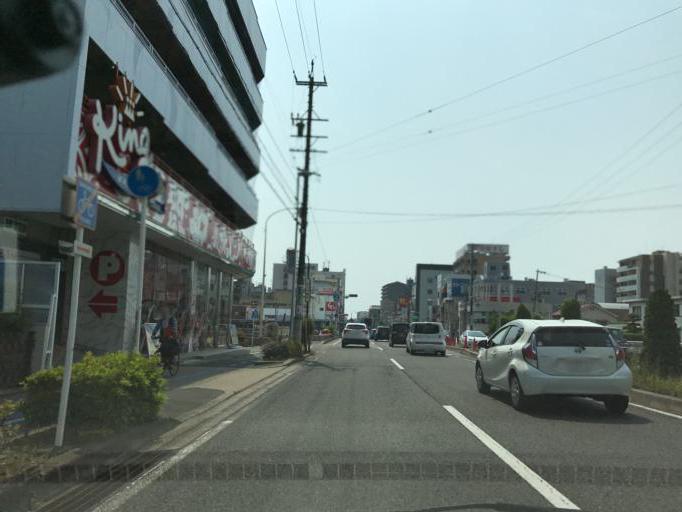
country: JP
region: Aichi
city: Nagoya-shi
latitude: 35.1177
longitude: 136.9399
